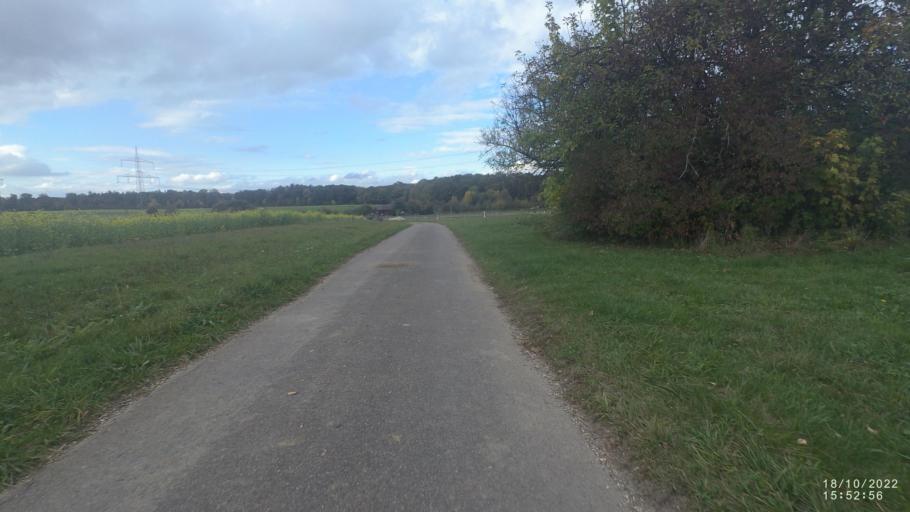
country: DE
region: Baden-Wuerttemberg
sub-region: Regierungsbezirk Stuttgart
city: Weilheim an der Teck
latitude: 48.6346
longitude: 9.5418
